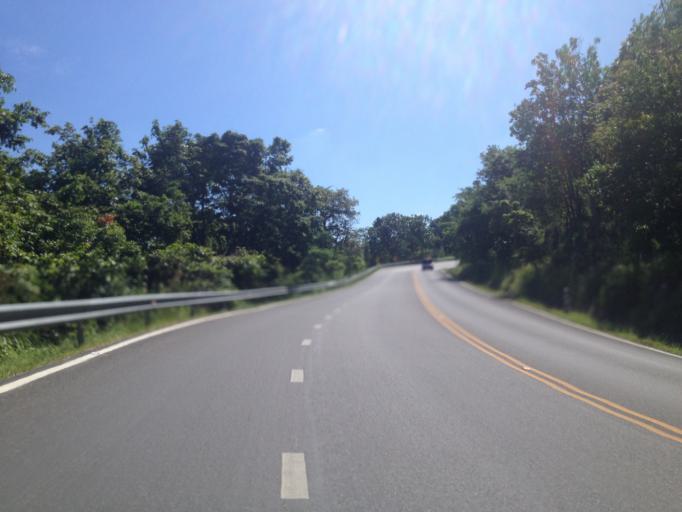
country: TH
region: Chiang Mai
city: Chiang Mai
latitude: 18.8144
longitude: 98.9429
